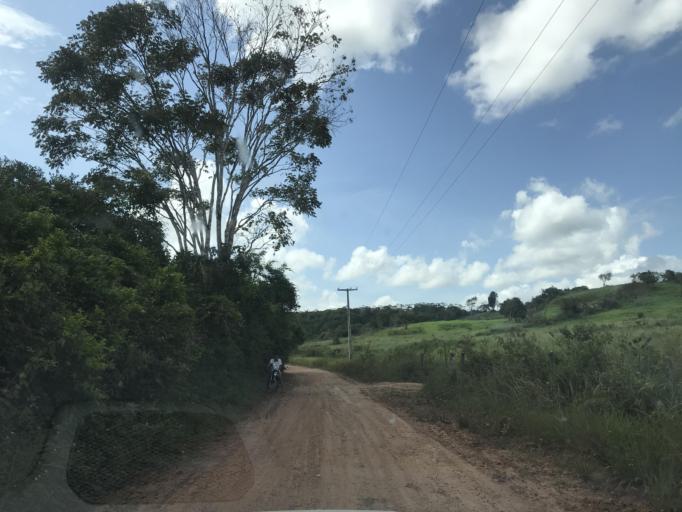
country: BR
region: Bahia
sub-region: Entre Rios
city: Entre Rios
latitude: -12.1745
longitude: -38.0627
